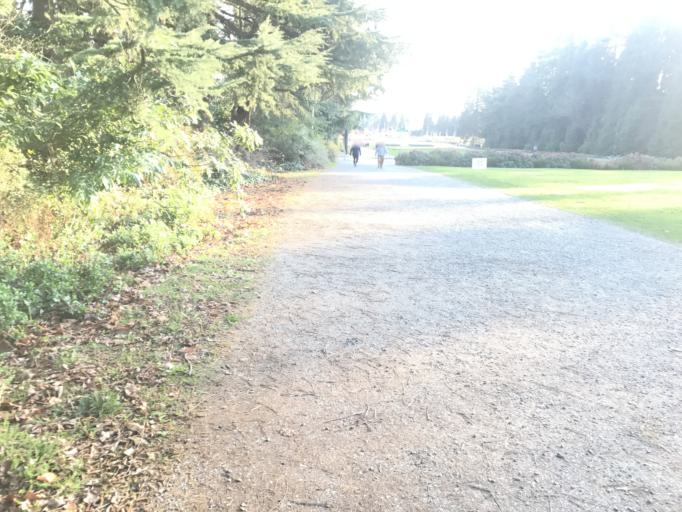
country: US
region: Washington
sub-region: King County
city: Seattle
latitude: 47.6527
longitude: -122.3068
